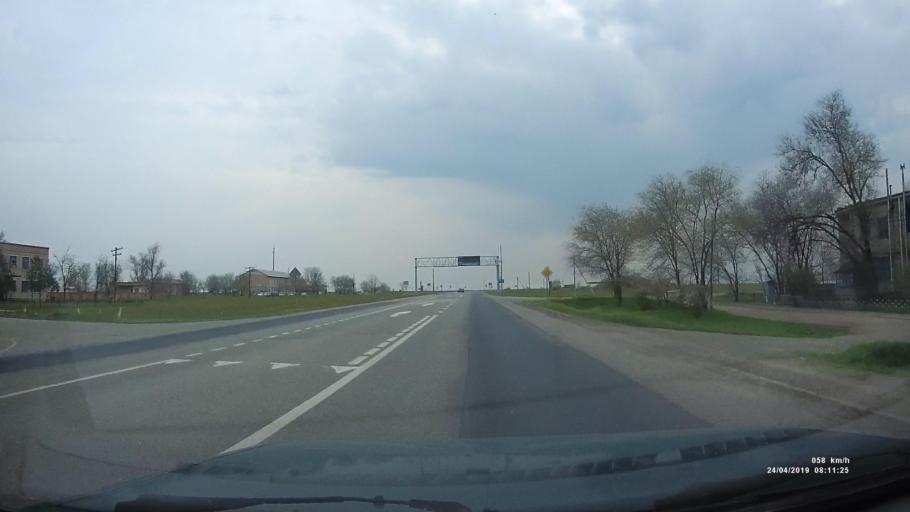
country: RU
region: Kalmykiya
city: Priyutnoye
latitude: 46.1020
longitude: 43.5278
